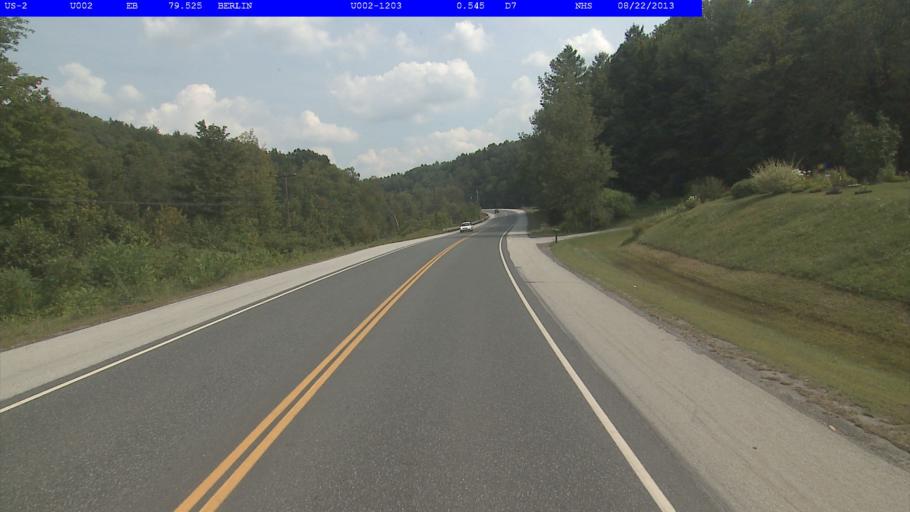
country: US
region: Vermont
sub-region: Washington County
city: Montpelier
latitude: 44.2403
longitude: -72.5325
